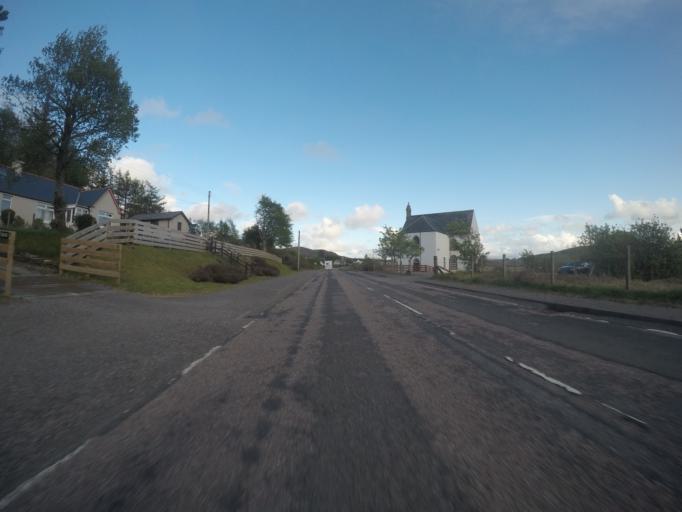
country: GB
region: Scotland
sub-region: Highland
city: Portree
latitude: 57.4827
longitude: -6.3041
